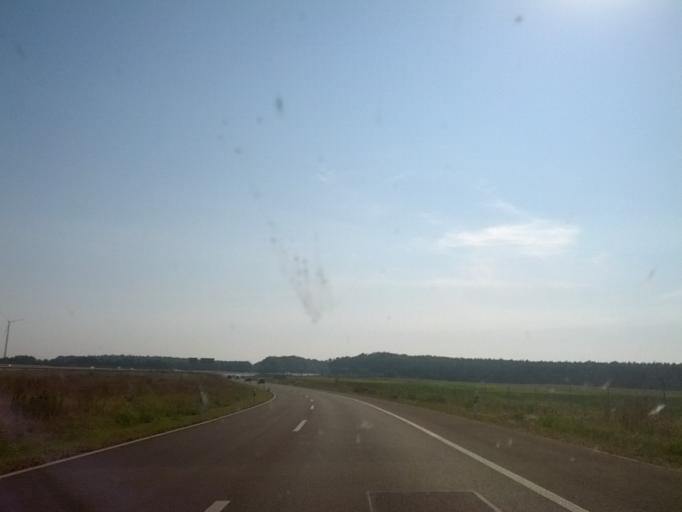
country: DE
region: Brandenburg
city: Ahrensfelde
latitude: 52.6117
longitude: 13.5692
